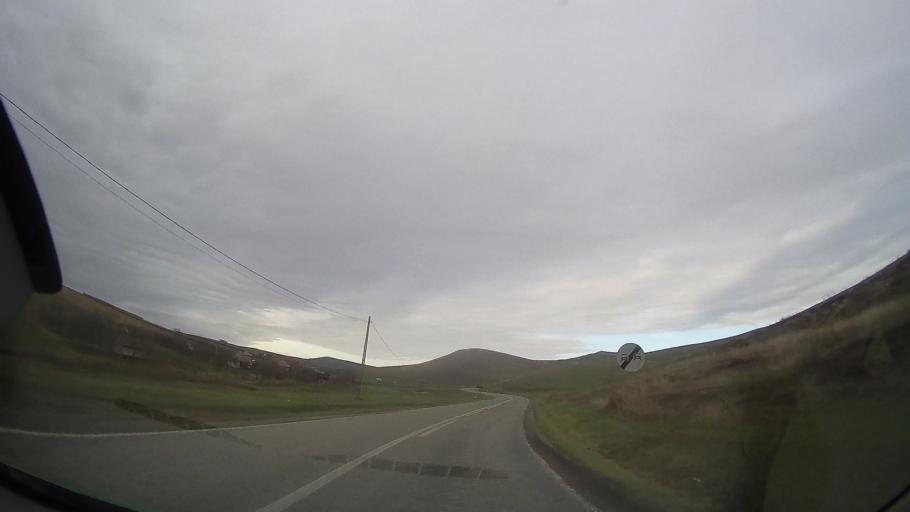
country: RO
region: Cluj
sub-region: Comuna Camarasu
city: Camarasu
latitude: 46.7957
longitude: 24.1765
